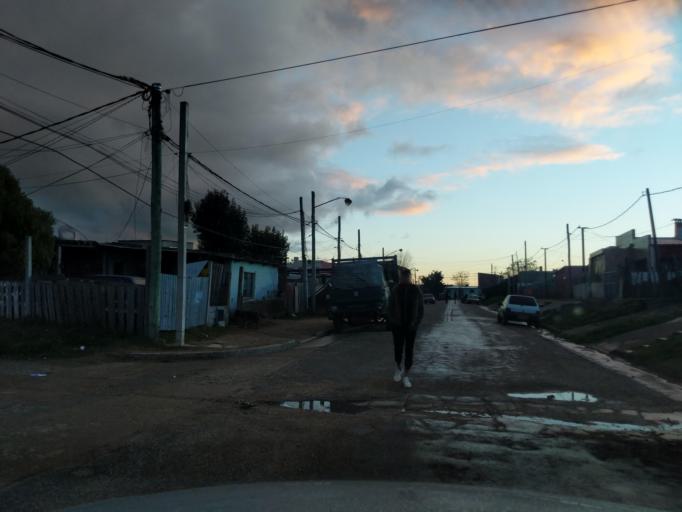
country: UY
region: Florida
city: Florida
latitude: -34.1090
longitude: -56.2075
